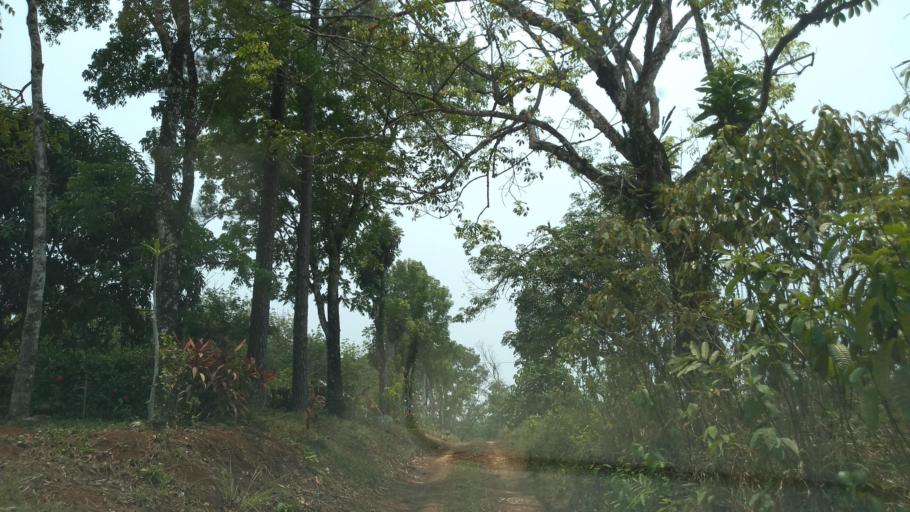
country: MX
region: Veracruz
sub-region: Tezonapa
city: Laguna Chica (Pueblo Nuevo)
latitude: 18.5119
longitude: -96.7619
